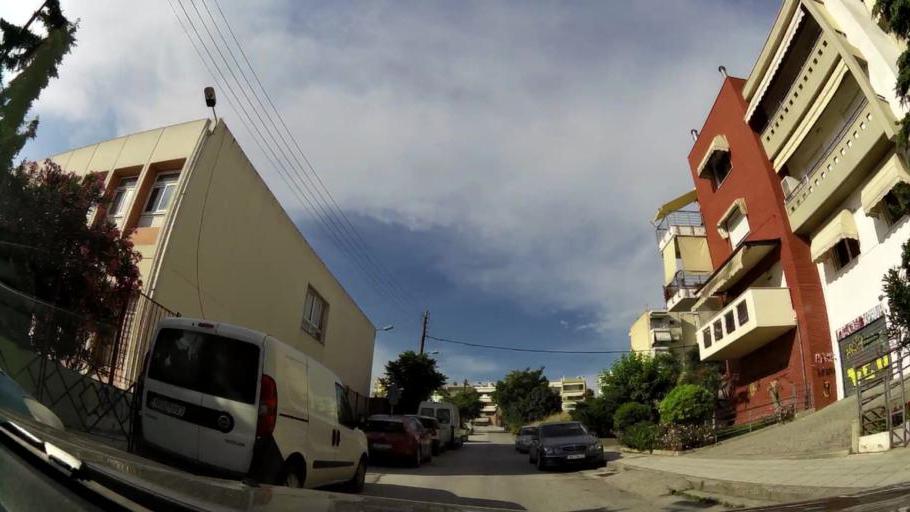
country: GR
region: Central Macedonia
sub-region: Nomos Thessalonikis
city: Kalamaria
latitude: 40.5739
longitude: 22.9569
